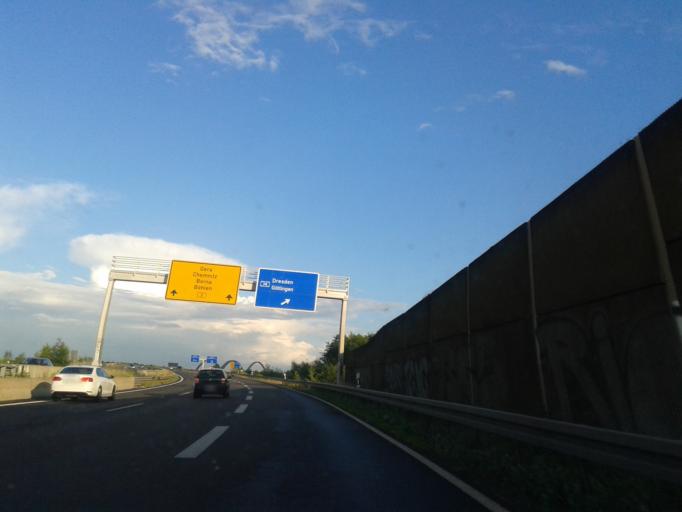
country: DE
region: Saxony
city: Markkleeberg
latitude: 51.2532
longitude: 12.3858
